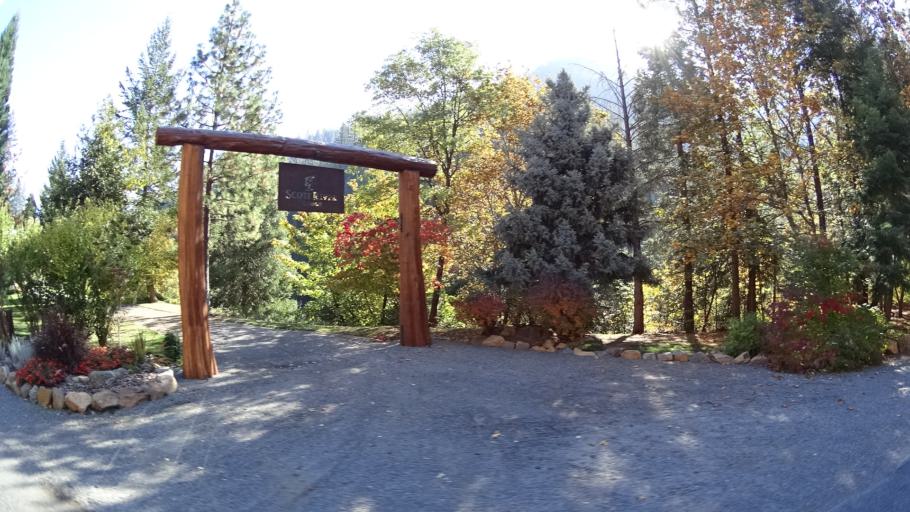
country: US
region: California
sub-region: Siskiyou County
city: Happy Camp
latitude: 41.6793
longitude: -123.1021
